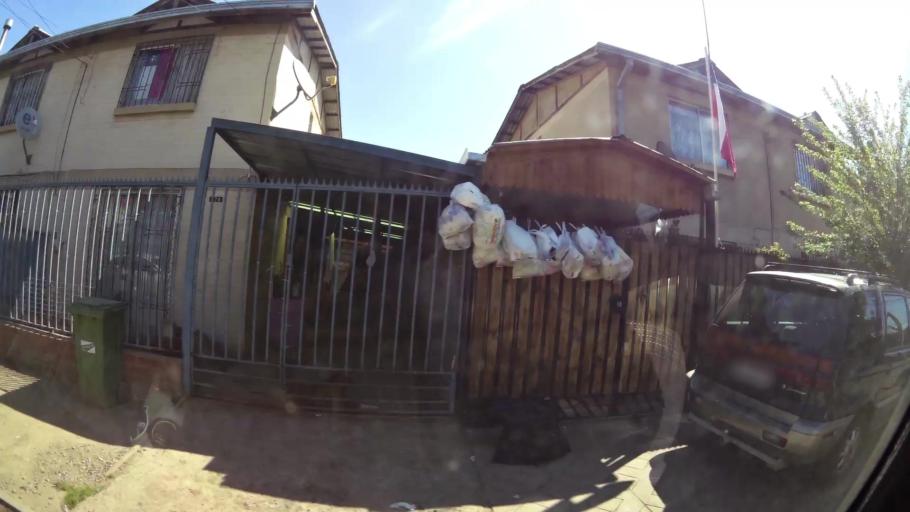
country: CL
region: Santiago Metropolitan
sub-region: Provincia de Talagante
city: Penaflor
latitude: -33.6096
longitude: -70.8886
